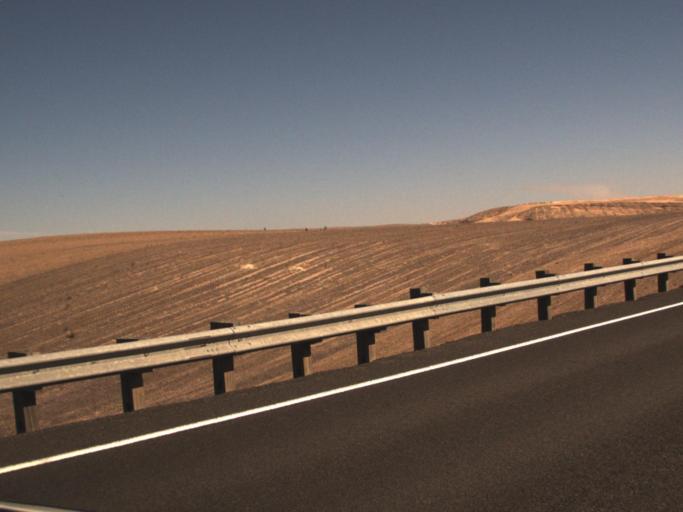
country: US
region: Washington
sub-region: Walla Walla County
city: Garrett
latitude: 46.2967
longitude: -118.5720
